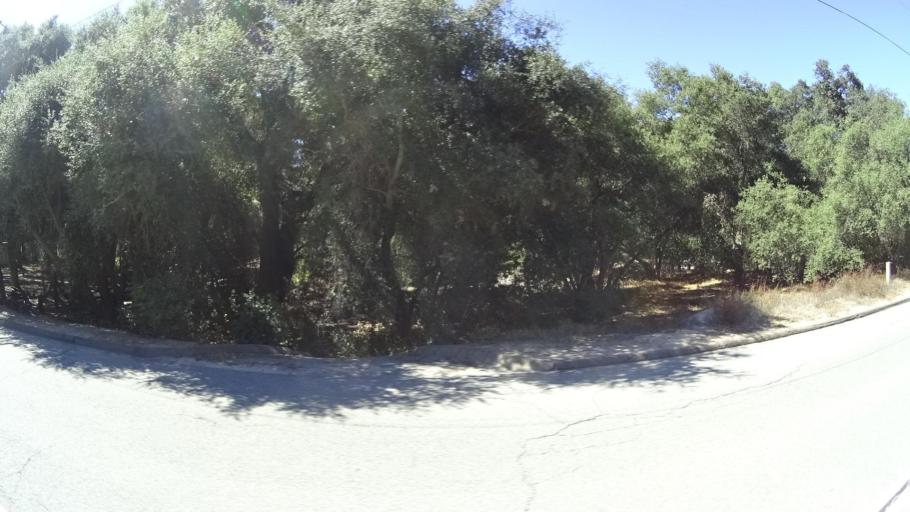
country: US
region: California
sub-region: San Diego County
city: Alpine
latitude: 32.7442
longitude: -116.7543
